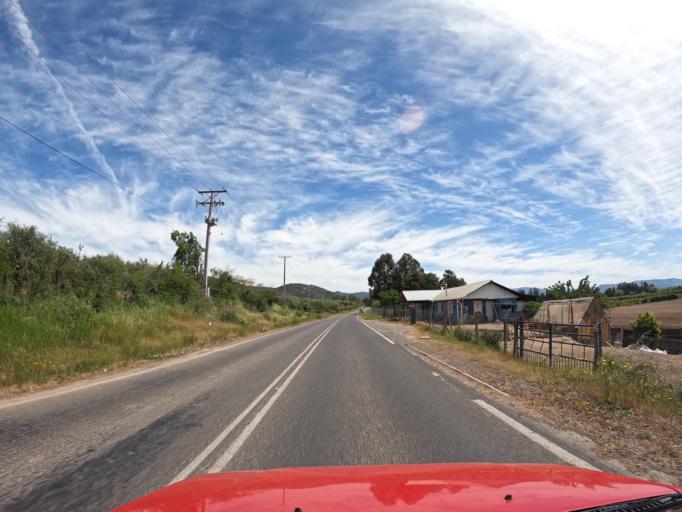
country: CL
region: Maule
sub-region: Provincia de Talca
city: Talca
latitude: -35.1144
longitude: -71.6373
